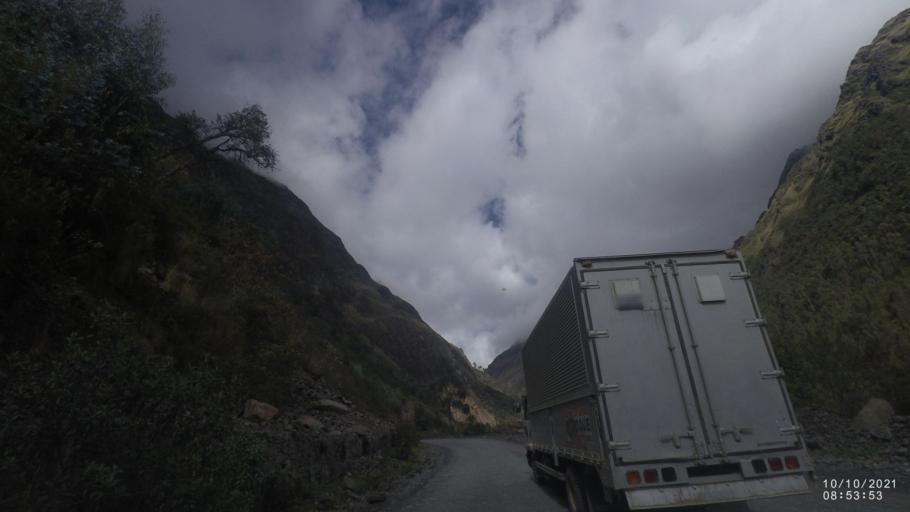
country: BO
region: La Paz
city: Quime
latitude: -16.9878
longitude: -67.2305
